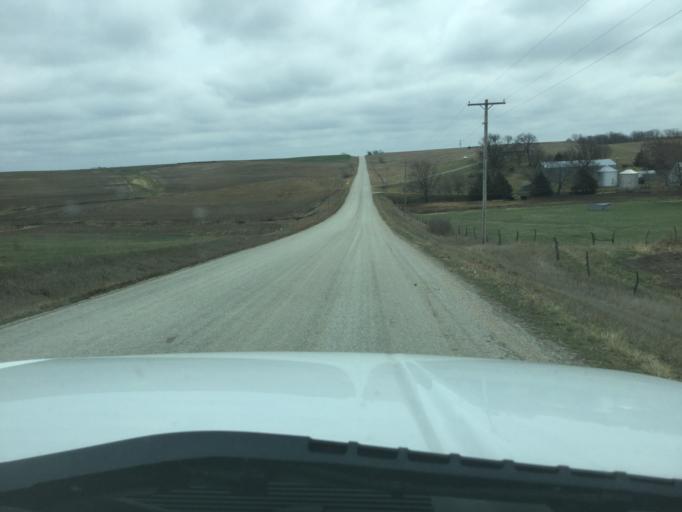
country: US
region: Kansas
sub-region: Nemaha County
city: Seneca
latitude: 39.7400
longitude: -96.0321
